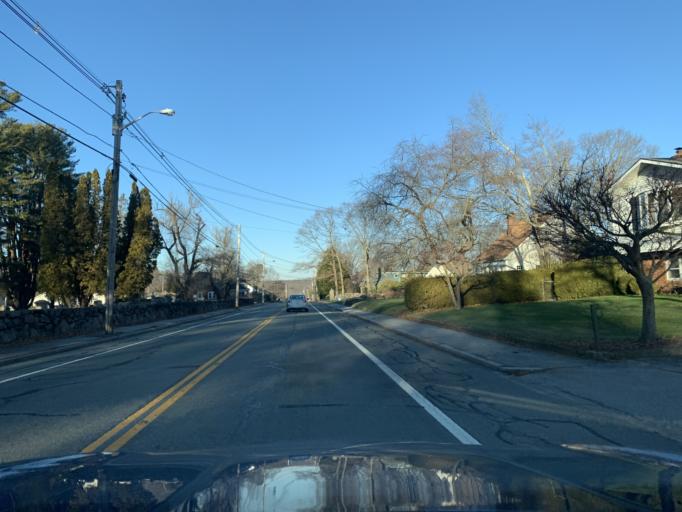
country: US
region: Rhode Island
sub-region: Kent County
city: West Warwick
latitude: 41.7140
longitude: -71.5352
